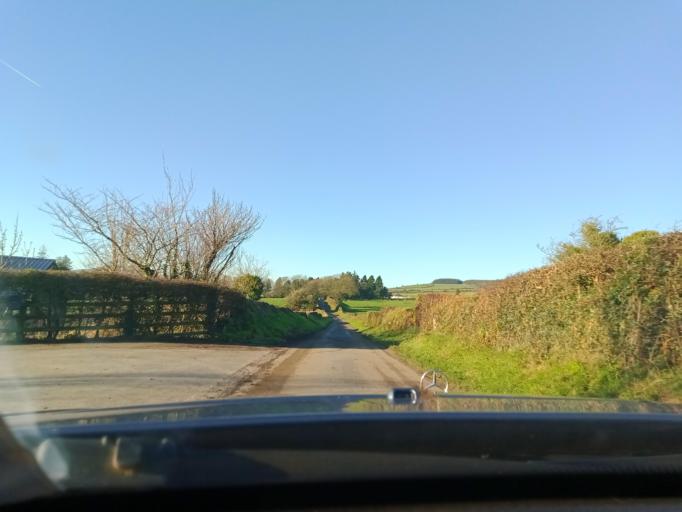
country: IE
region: Leinster
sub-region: Kilkenny
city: Callan
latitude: 52.4605
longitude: -7.4072
